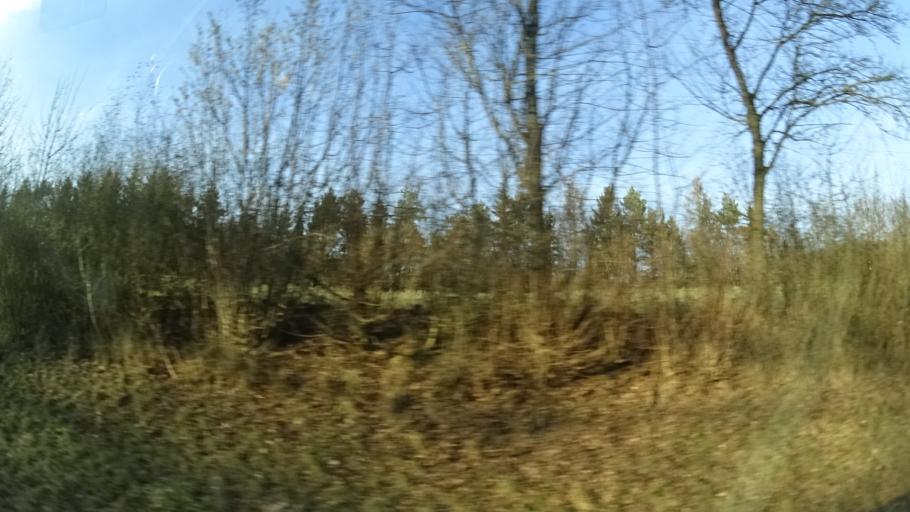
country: DE
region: Hesse
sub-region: Regierungsbezirk Darmstadt
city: Schluchtern
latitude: 50.3190
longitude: 9.6051
